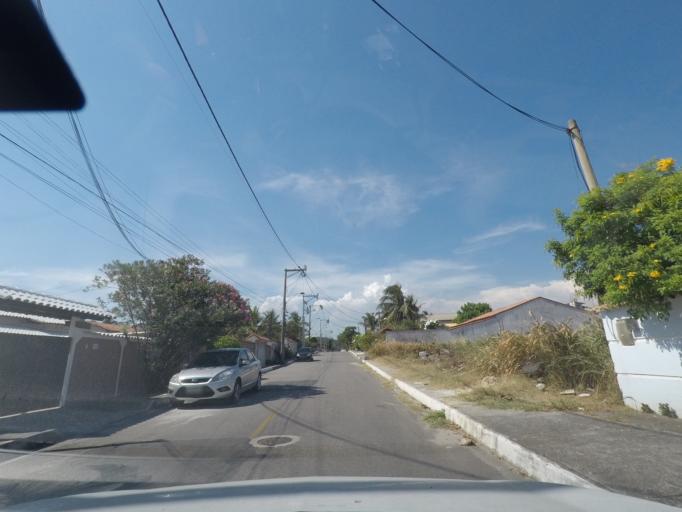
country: BR
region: Rio de Janeiro
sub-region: Niteroi
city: Niteroi
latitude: -22.9664
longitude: -42.9702
